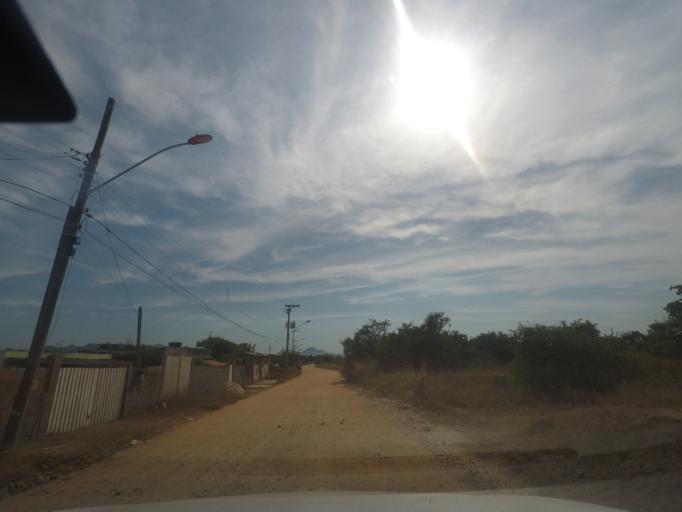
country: BR
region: Rio de Janeiro
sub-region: Marica
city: Marica
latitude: -22.9600
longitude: -42.8379
